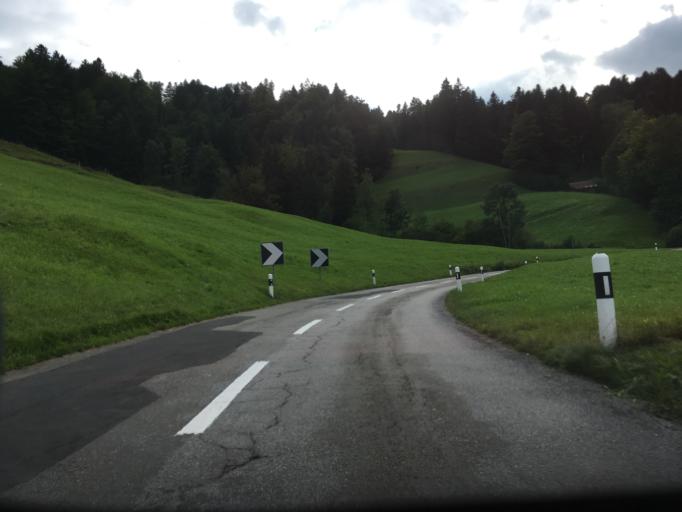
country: CH
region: Thurgau
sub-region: Muenchwilen District
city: Fischingen
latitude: 47.3644
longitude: 8.9742
